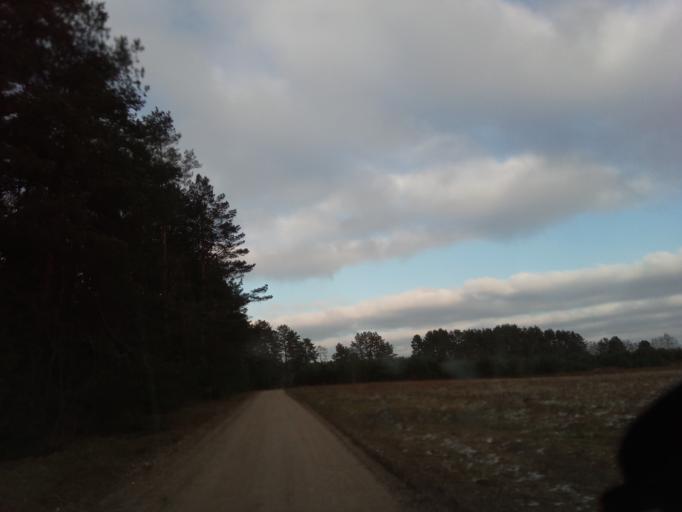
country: LT
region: Alytaus apskritis
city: Druskininkai
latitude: 53.9461
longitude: 24.2827
